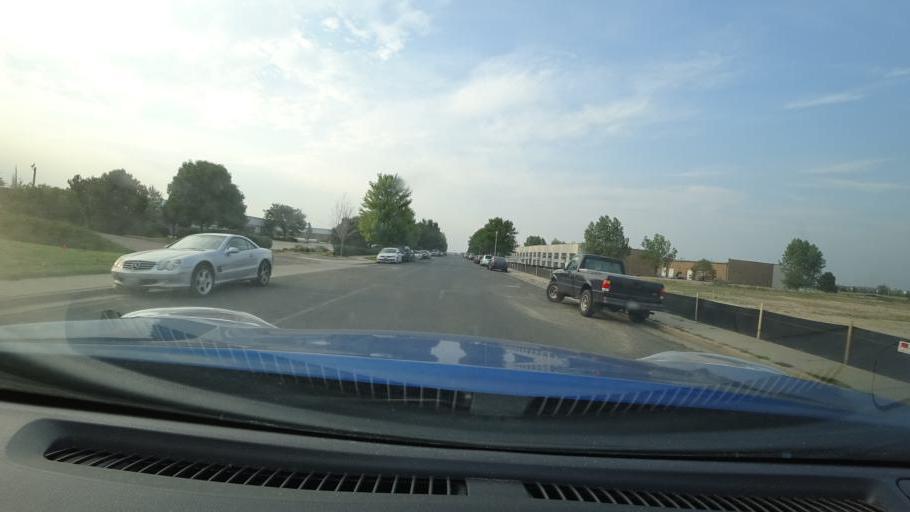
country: US
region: Colorado
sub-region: Adams County
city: Aurora
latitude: 39.7299
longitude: -104.7833
